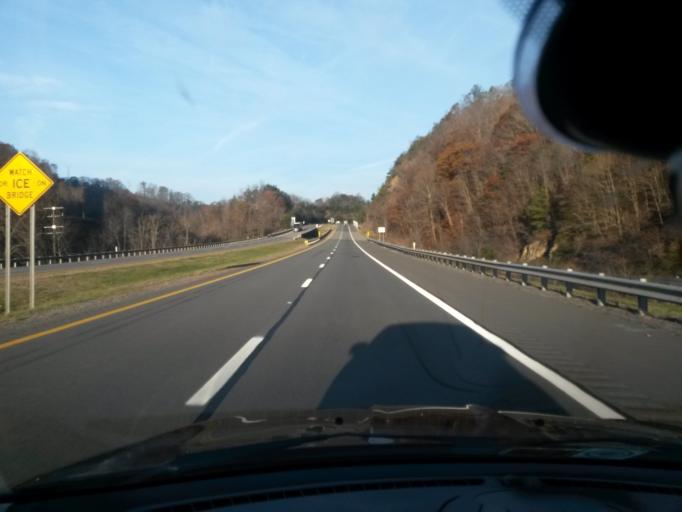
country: US
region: West Virginia
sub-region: Greenbrier County
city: Lewisburg
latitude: 37.7725
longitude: -80.3743
